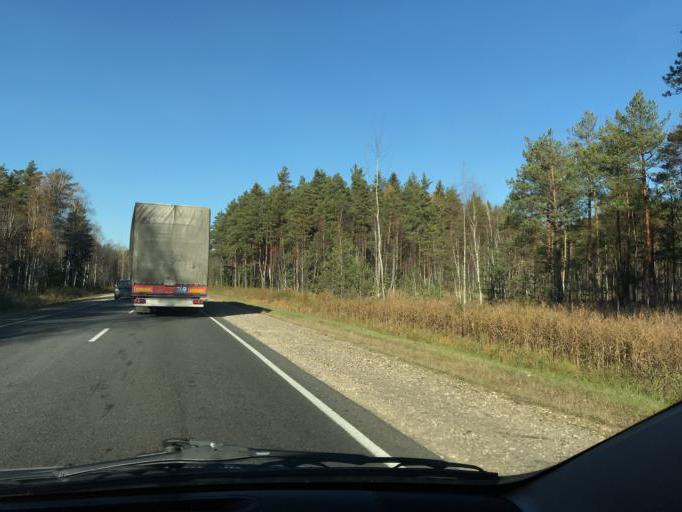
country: BY
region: Vitebsk
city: Polatsk
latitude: 55.5175
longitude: 28.7360
